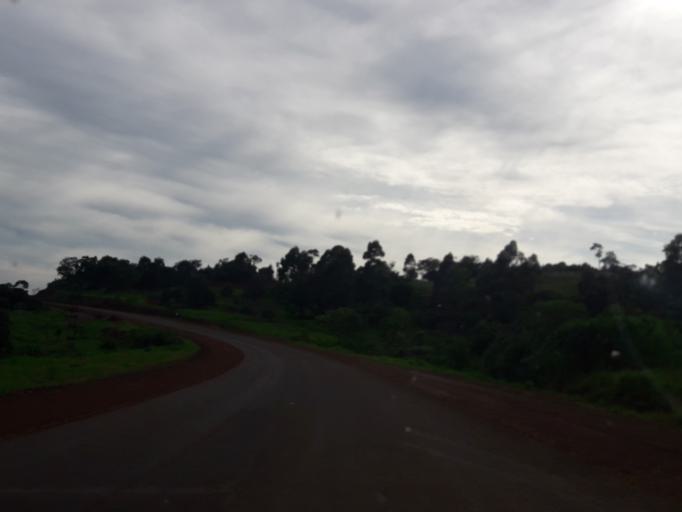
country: AR
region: Misiones
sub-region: Departamento de San Pedro
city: San Pedro
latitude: -26.5125
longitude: -53.9265
